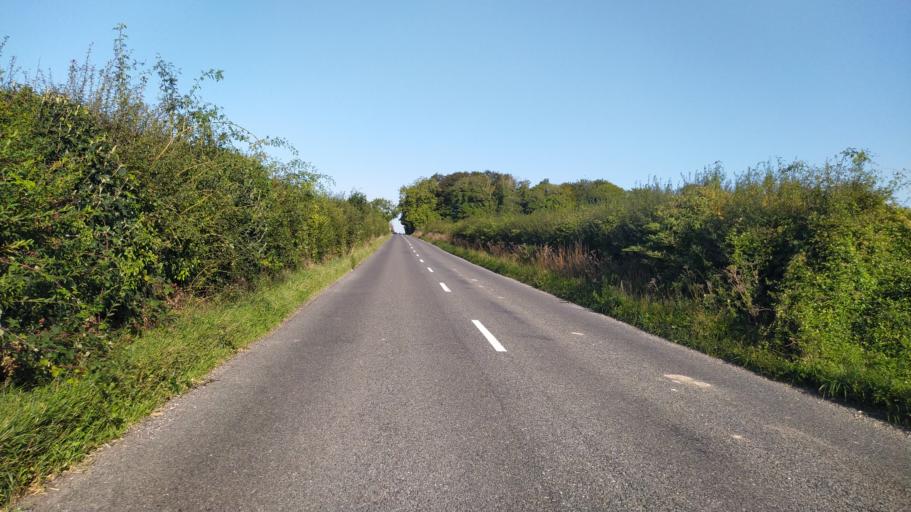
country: GB
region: England
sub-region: Hampshire
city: Abbotts Ann
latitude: 51.1561
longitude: -1.5557
